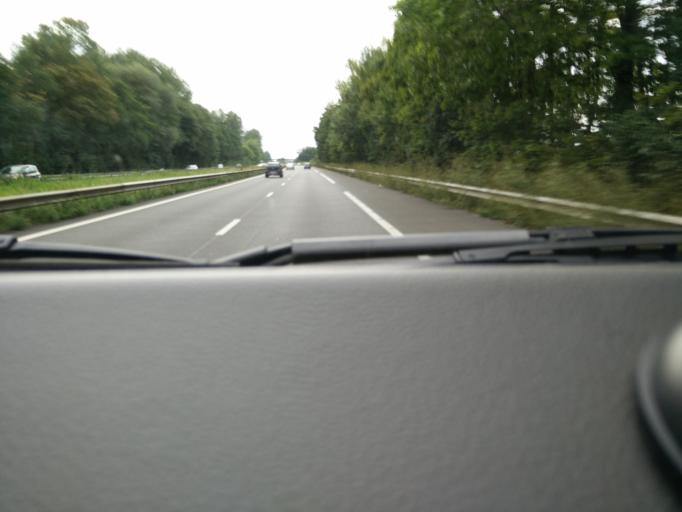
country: FR
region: Nord-Pas-de-Calais
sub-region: Departement du Nord
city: Sameon
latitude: 50.4537
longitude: 3.3269
